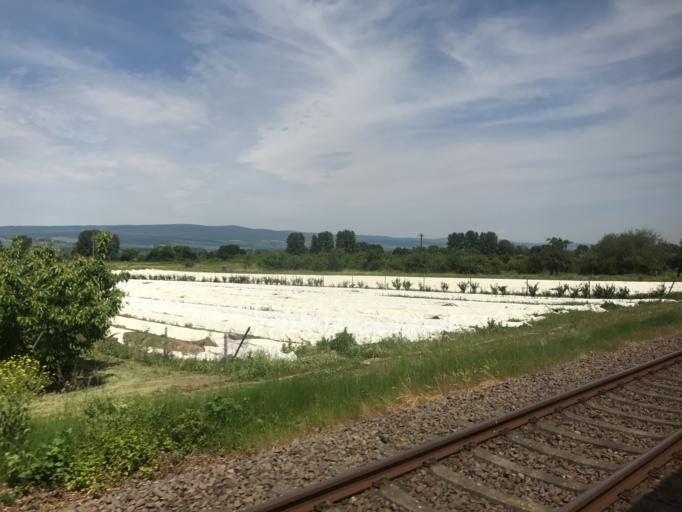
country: DE
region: Rheinland-Pfalz
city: Gau-Algesheim
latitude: 49.9551
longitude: 7.9982
